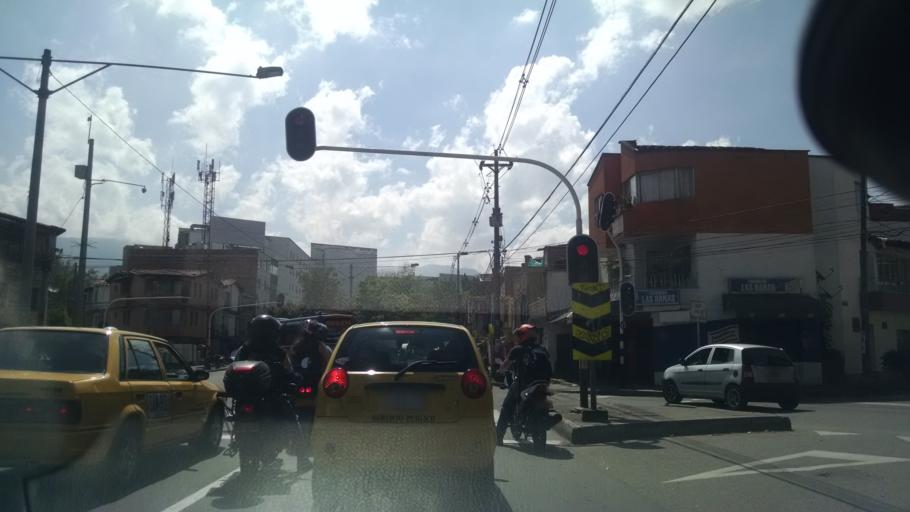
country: CO
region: Antioquia
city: Itagui
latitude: 6.2257
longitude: -75.6004
